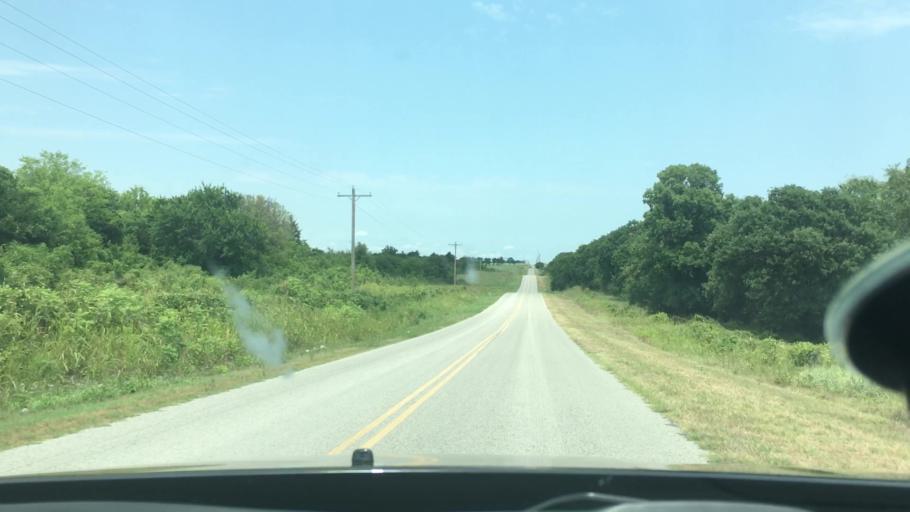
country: US
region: Oklahoma
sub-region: Love County
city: Marietta
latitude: 33.8987
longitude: -97.3521
